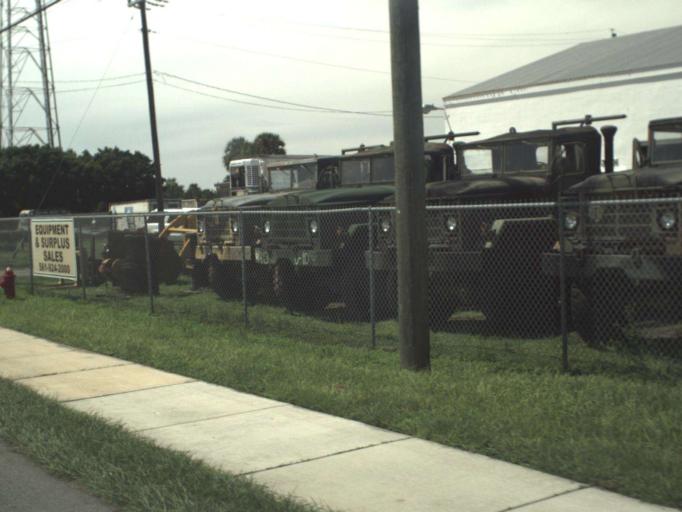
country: US
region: Florida
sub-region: Palm Beach County
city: Pahokee
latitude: 26.8475
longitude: -80.6418
